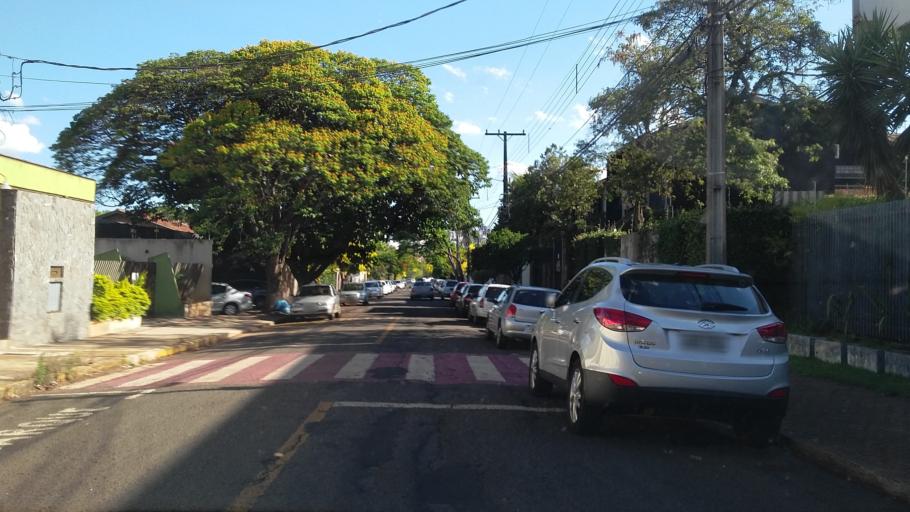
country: BR
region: Parana
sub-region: Londrina
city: Londrina
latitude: -23.3155
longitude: -51.1766
